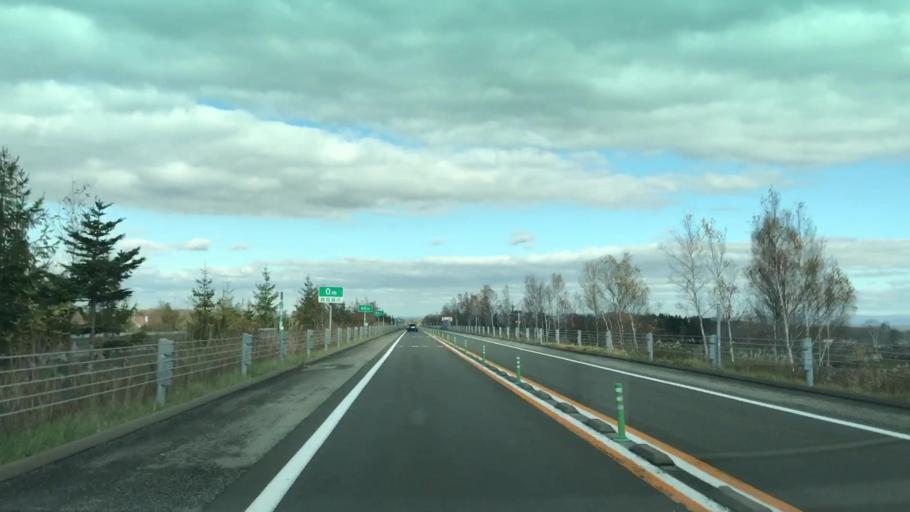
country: JP
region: Hokkaido
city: Chitose
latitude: 42.8680
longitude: 141.6112
